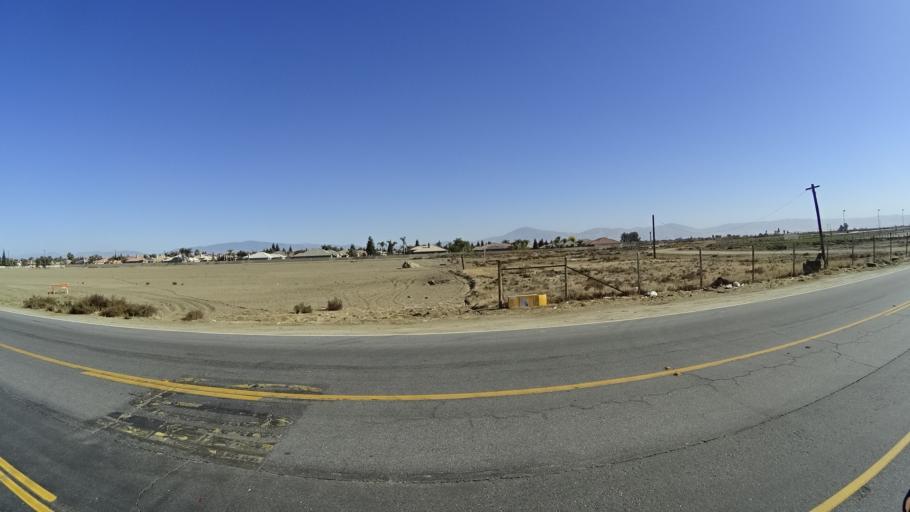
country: US
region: California
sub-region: Kern County
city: Greenfield
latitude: 35.2716
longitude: -119.0569
